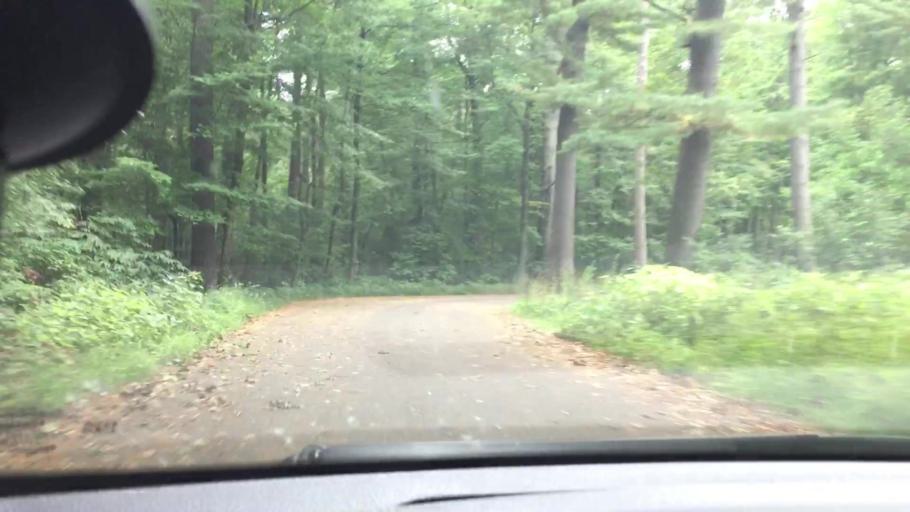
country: US
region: Wisconsin
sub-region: Chippewa County
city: Chippewa Falls
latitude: 44.9644
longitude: -91.4024
